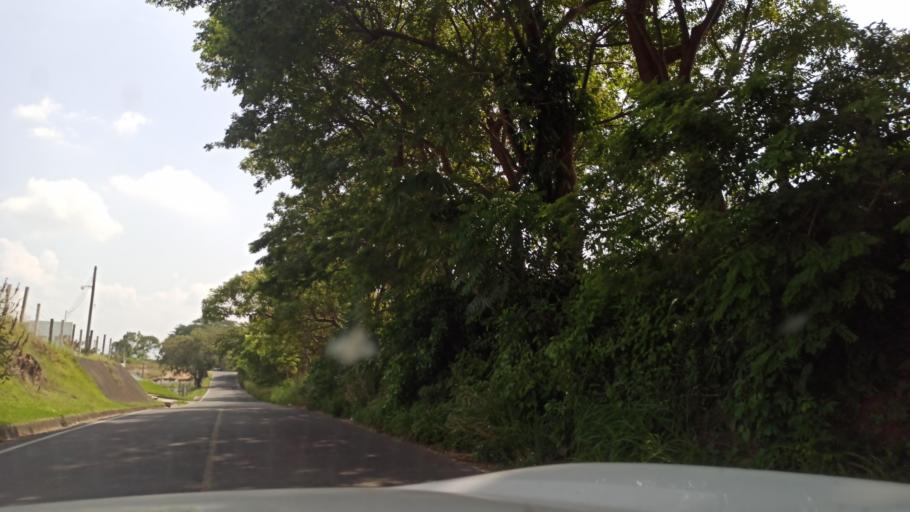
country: MX
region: Veracruz
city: Martinez de la Torre
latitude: 20.0843
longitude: -97.0750
